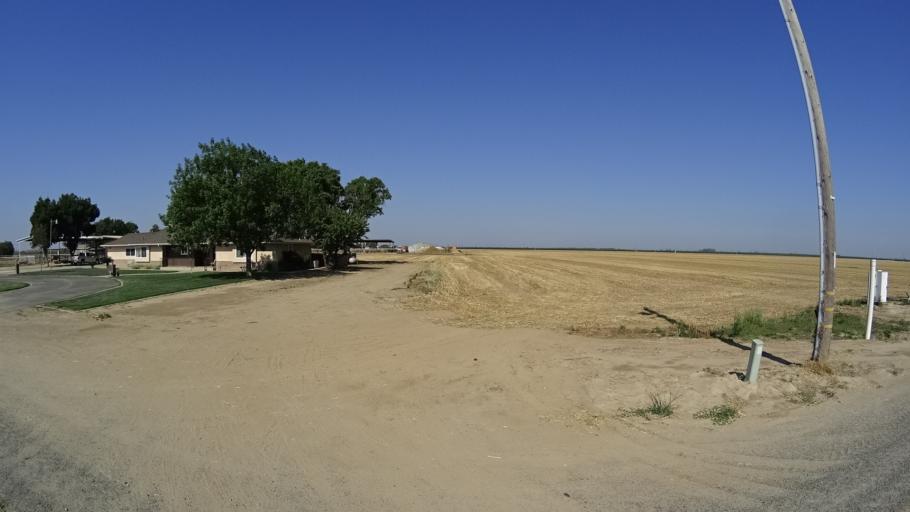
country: US
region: California
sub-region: Kings County
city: Hanford
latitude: 36.3737
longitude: -119.5649
